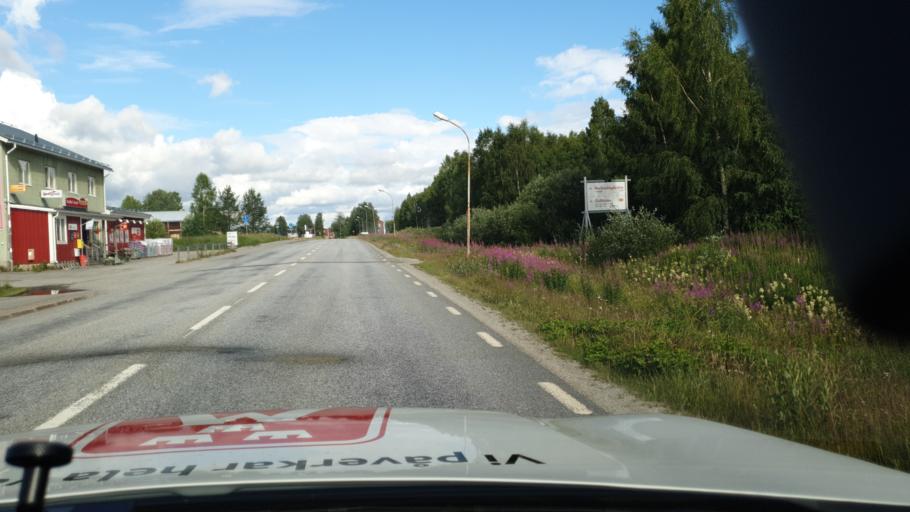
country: SE
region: Vaesterbotten
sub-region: Bjurholms Kommun
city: Bjurholm
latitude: 64.2510
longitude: 19.3096
